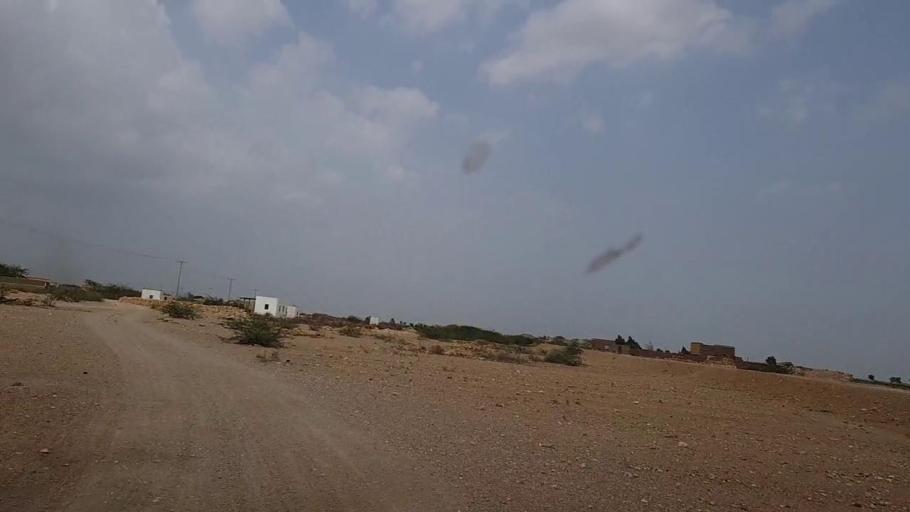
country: PK
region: Sindh
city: Kotri
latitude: 25.2861
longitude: 68.2164
